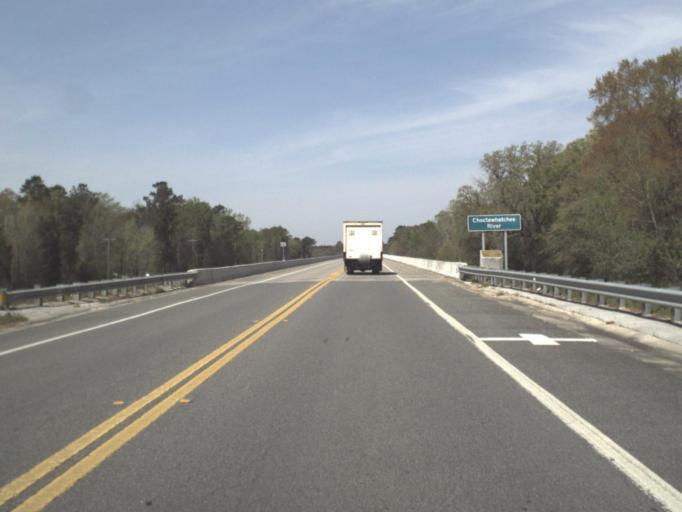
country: US
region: Florida
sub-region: Holmes County
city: Bonifay
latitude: 30.7736
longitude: -85.8224
